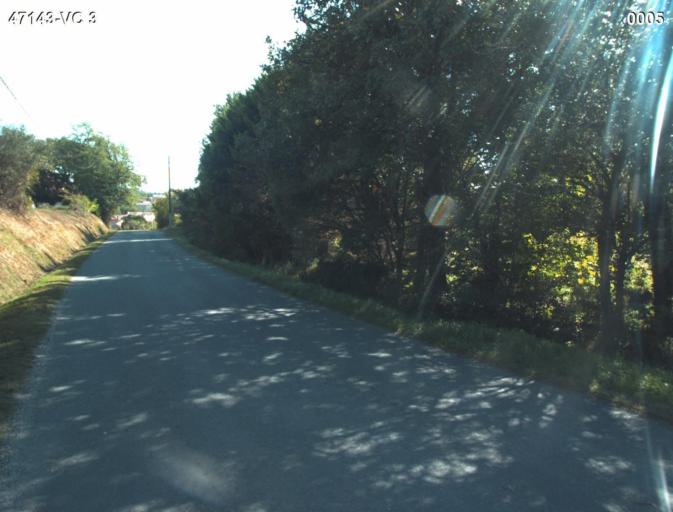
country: FR
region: Aquitaine
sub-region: Departement du Lot-et-Garonne
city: Lavardac
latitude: 44.1838
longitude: 0.2947
